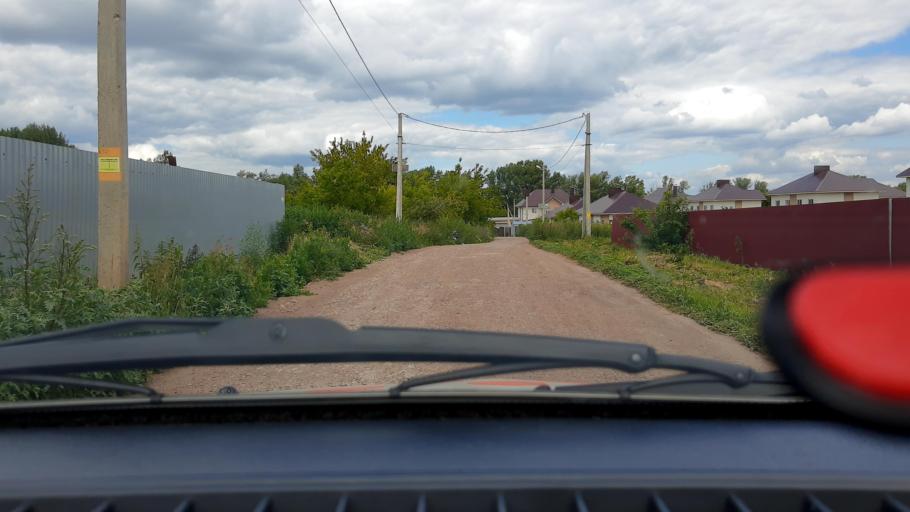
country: RU
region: Bashkortostan
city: Avdon
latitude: 54.5008
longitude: 55.8968
